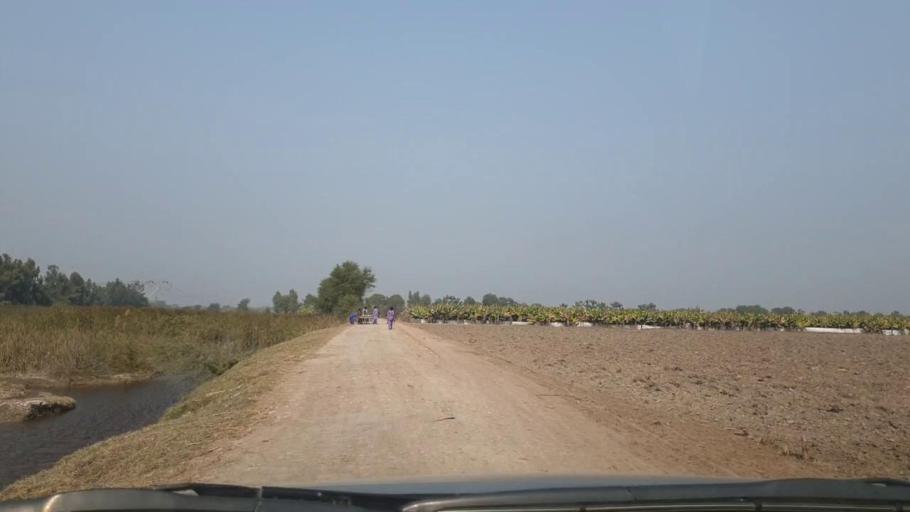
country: PK
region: Sindh
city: Matiari
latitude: 25.6585
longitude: 68.5435
